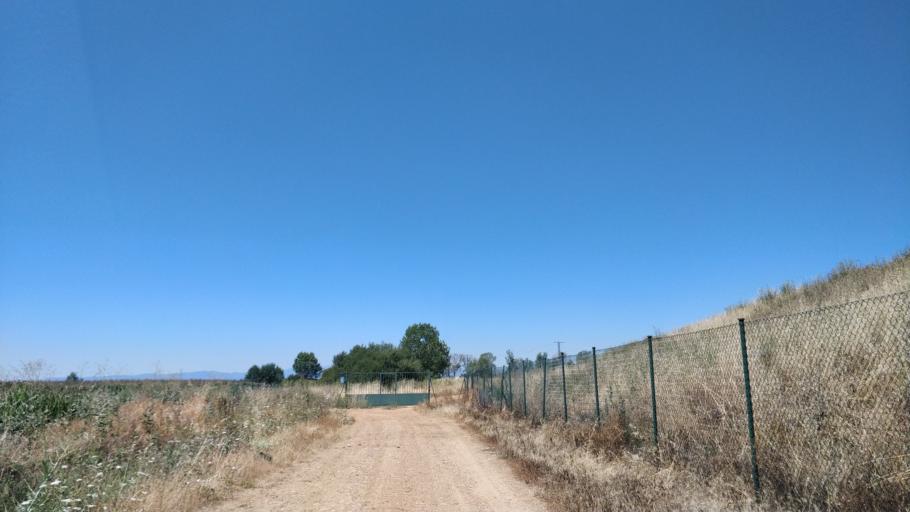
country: ES
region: Castille and Leon
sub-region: Provincia de Leon
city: Bustillo del Paramo
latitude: 42.4786
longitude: -5.8078
